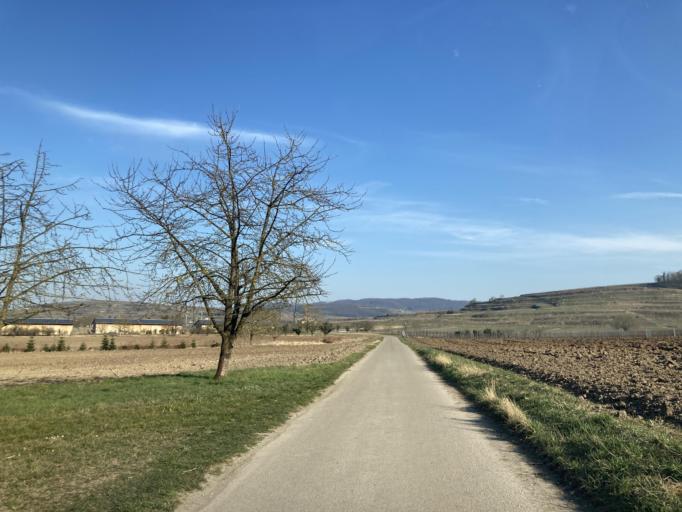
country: DE
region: Baden-Wuerttemberg
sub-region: Freiburg Region
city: Sasbach
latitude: 48.1185
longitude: 7.5869
